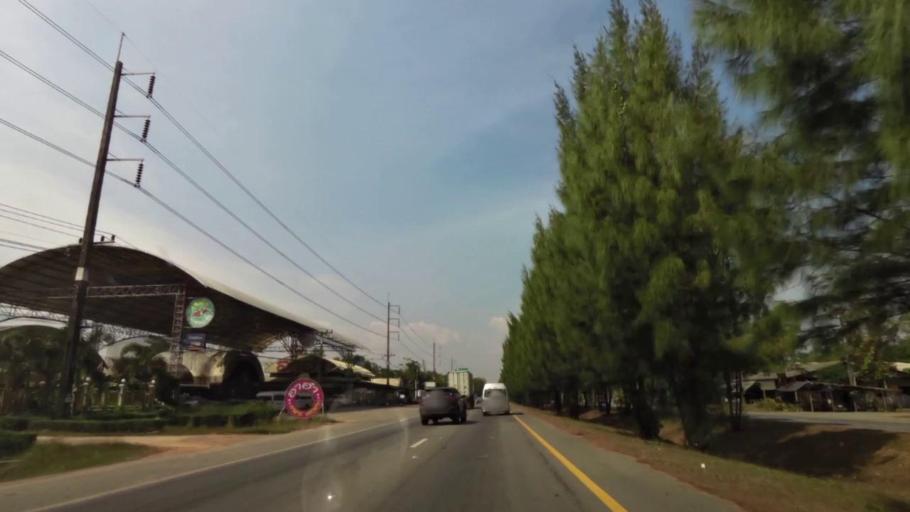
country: TH
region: Chanthaburi
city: Chanthaburi
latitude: 12.6523
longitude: 102.1274
